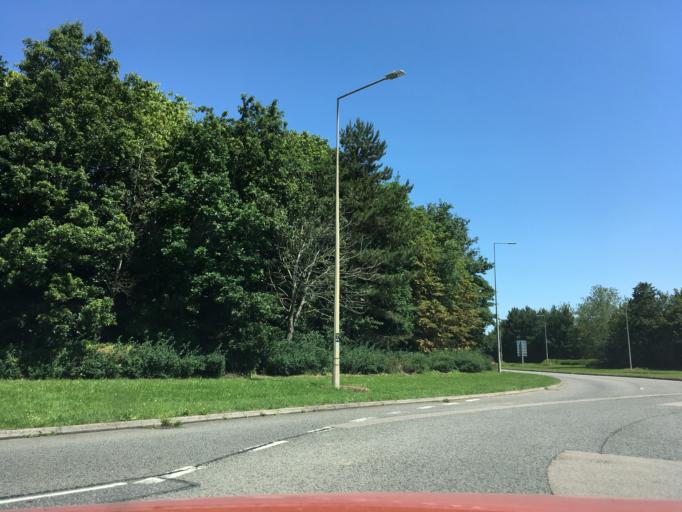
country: GB
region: England
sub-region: Milton Keynes
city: Shenley Church End
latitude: 52.0174
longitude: -0.7853
